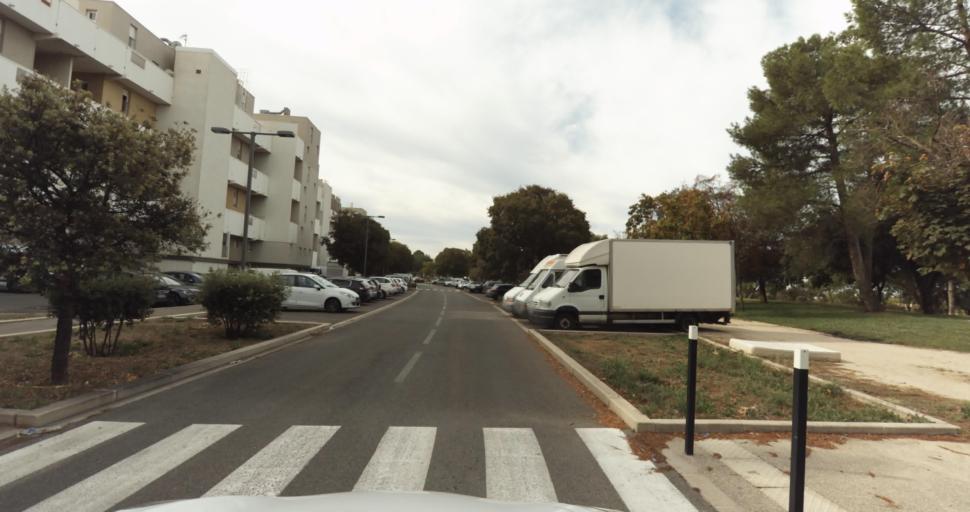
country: FR
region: Provence-Alpes-Cote d'Azur
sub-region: Departement des Bouches-du-Rhone
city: Miramas
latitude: 43.5971
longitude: 5.0063
